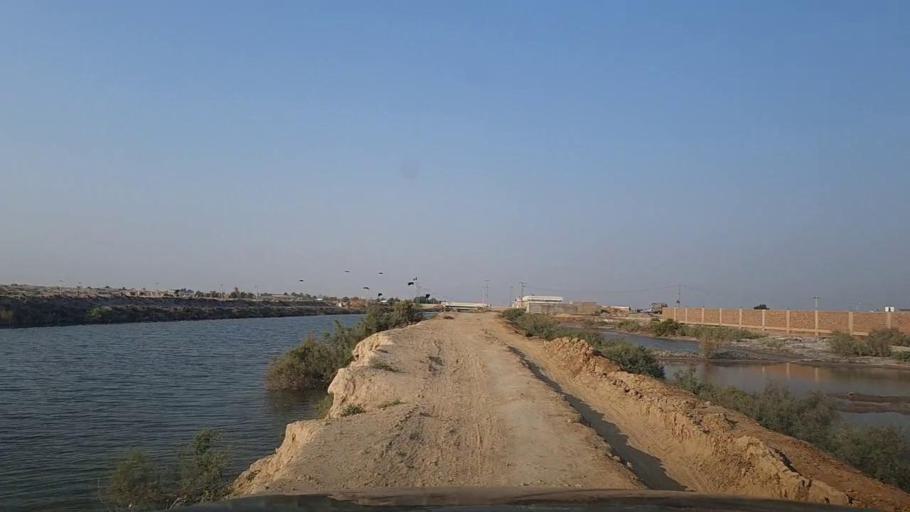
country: PK
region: Sindh
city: Thatta
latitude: 24.7465
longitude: 67.9072
